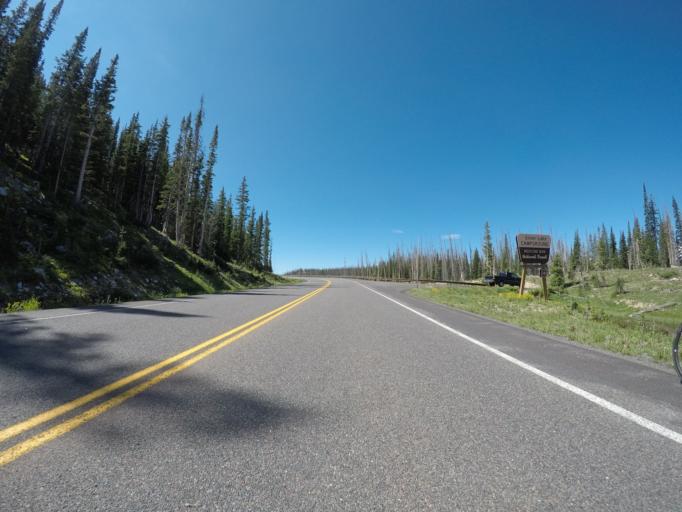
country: US
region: Wyoming
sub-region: Carbon County
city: Saratoga
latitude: 41.3153
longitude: -106.3590
